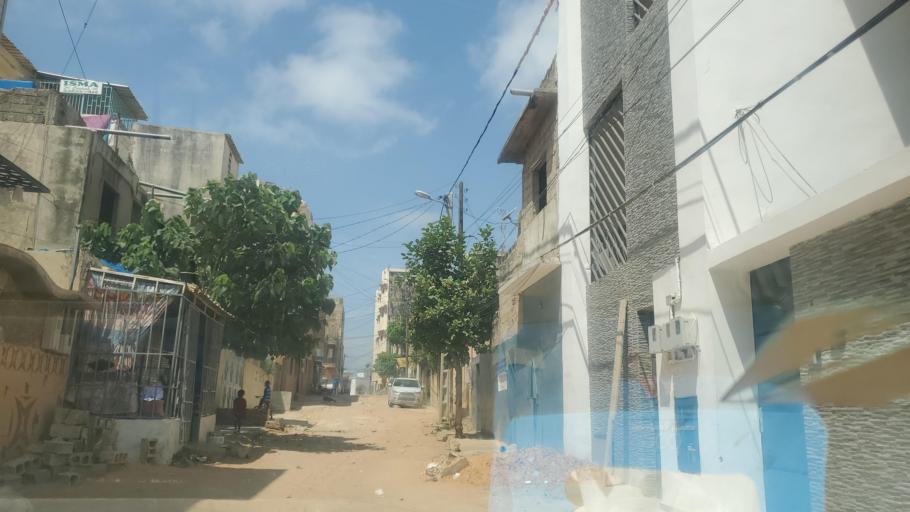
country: SN
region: Dakar
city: Grand Dakar
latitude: 14.7300
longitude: -17.4553
